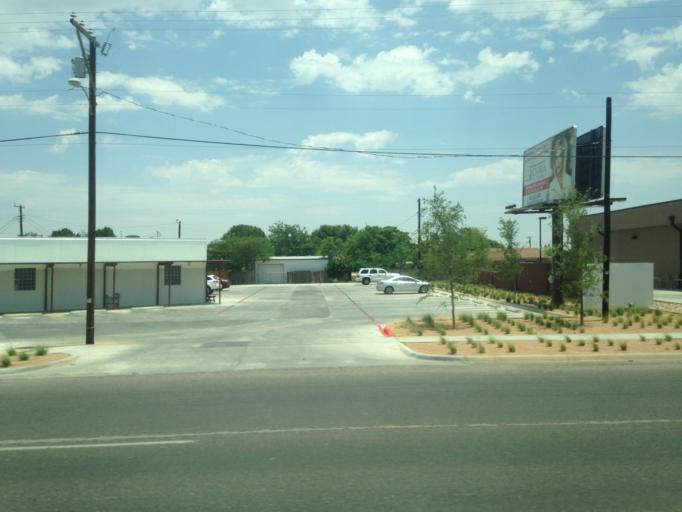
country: US
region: Texas
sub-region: Midland County
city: Midland
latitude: 32.0304
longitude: -102.0839
